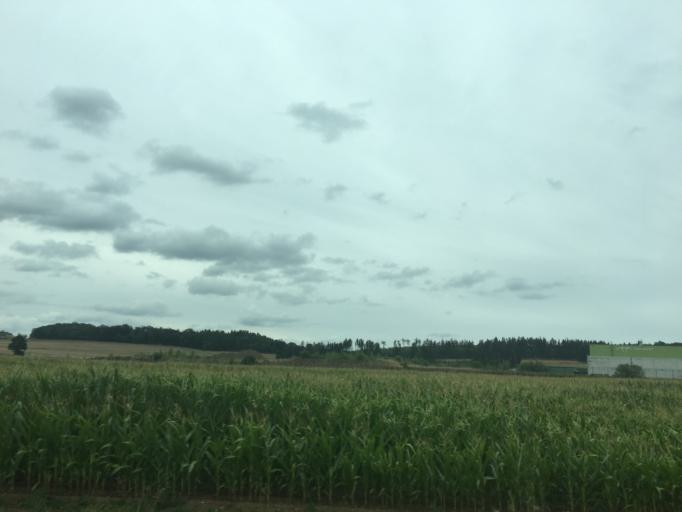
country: DE
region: Bavaria
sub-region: Upper Franconia
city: Trogen
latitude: 50.3427
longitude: 11.9592
